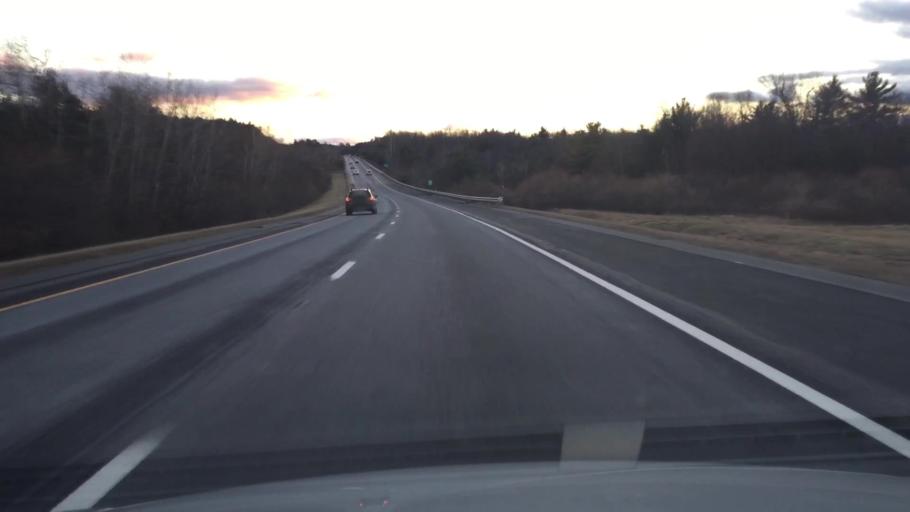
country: US
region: Massachusetts
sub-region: Worcester County
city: West Boylston
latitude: 42.3871
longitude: -71.8174
